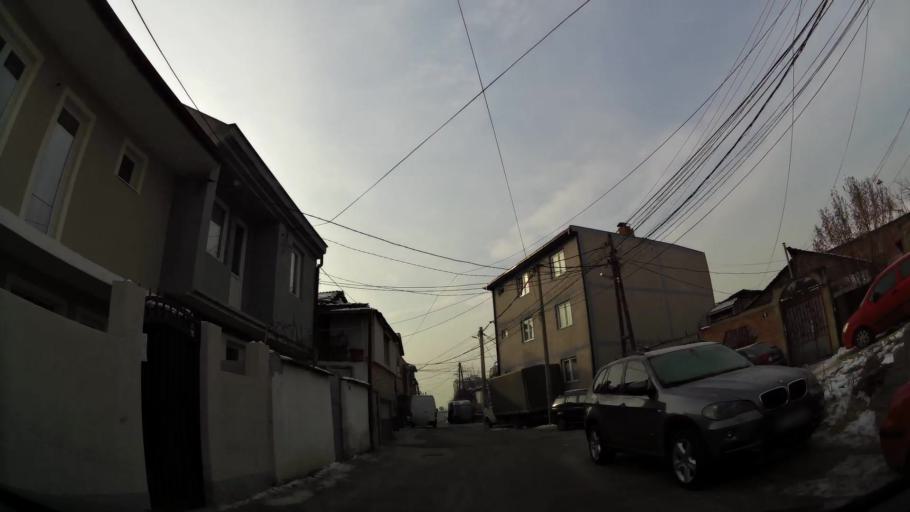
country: MK
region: Cair
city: Cair
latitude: 42.0155
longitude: 21.4390
